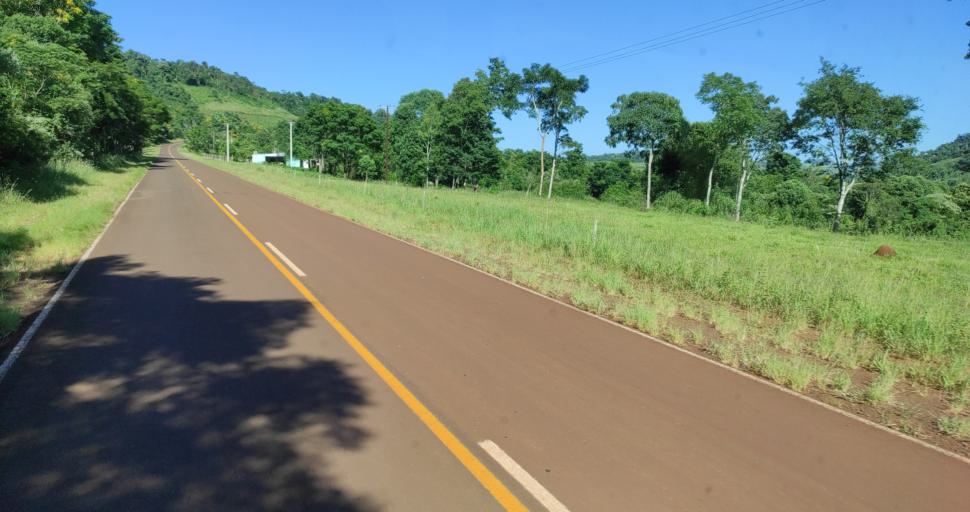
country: AR
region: Misiones
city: El Soberbio
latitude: -27.2243
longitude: -54.0556
